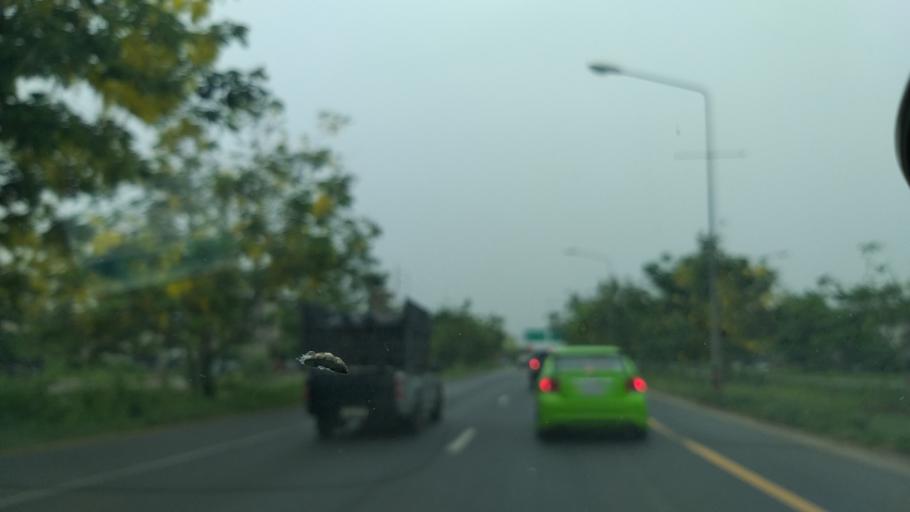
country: TH
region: Chon Buri
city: Ko Chan
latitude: 13.3852
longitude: 101.2785
